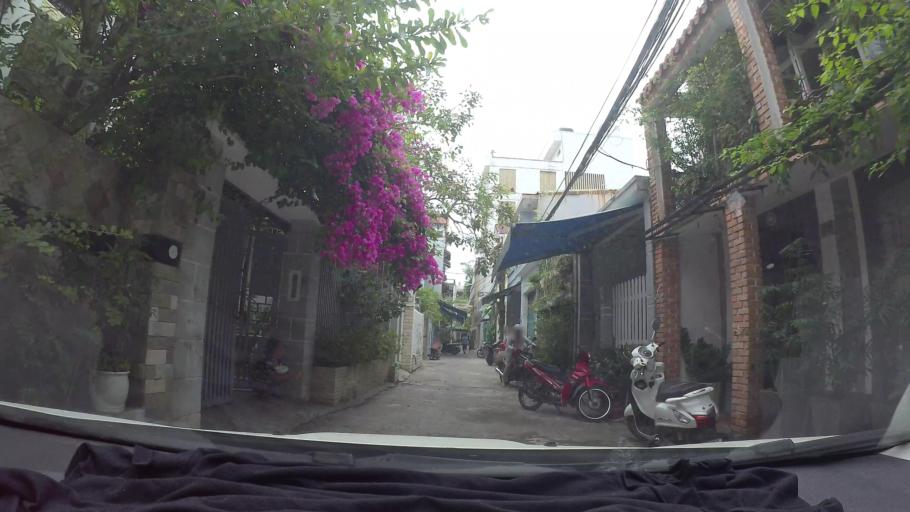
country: VN
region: Da Nang
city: Cam Le
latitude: 16.0305
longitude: 108.2258
